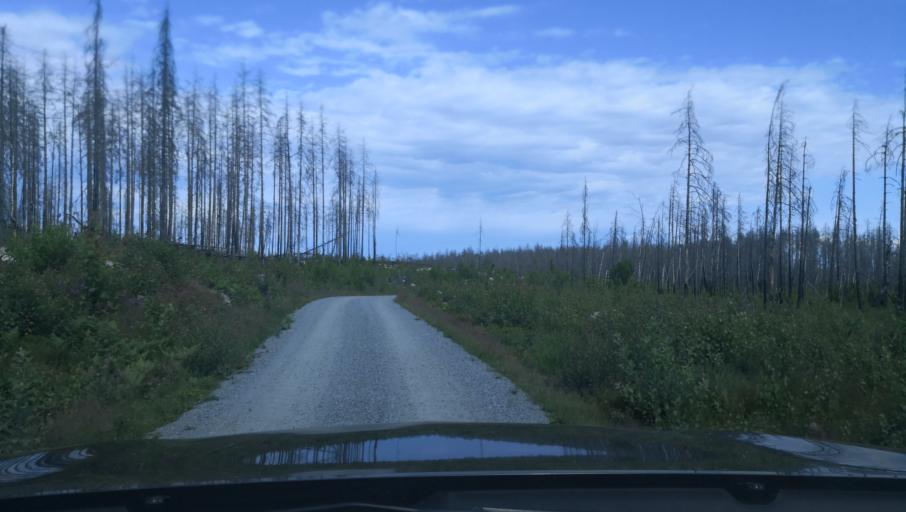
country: SE
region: Vaestmanland
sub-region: Surahammars Kommun
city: Ramnas
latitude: 59.9209
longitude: 16.1639
